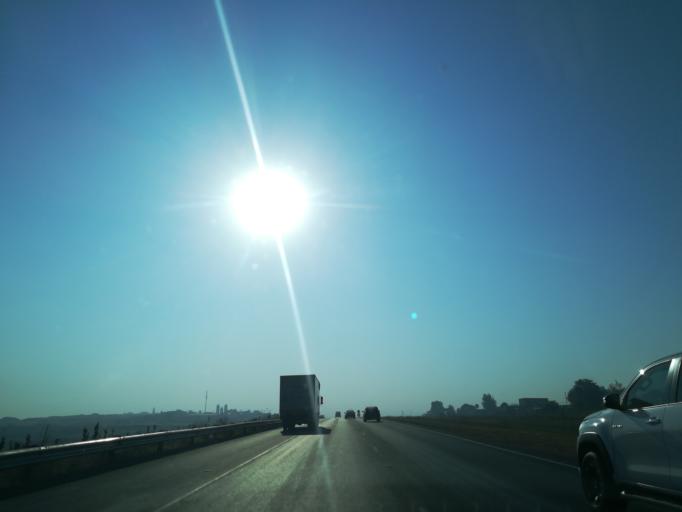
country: ZA
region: Gauteng
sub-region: City of Johannesburg Metropolitan Municipality
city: Diepsloot
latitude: -25.9272
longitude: 28.0006
